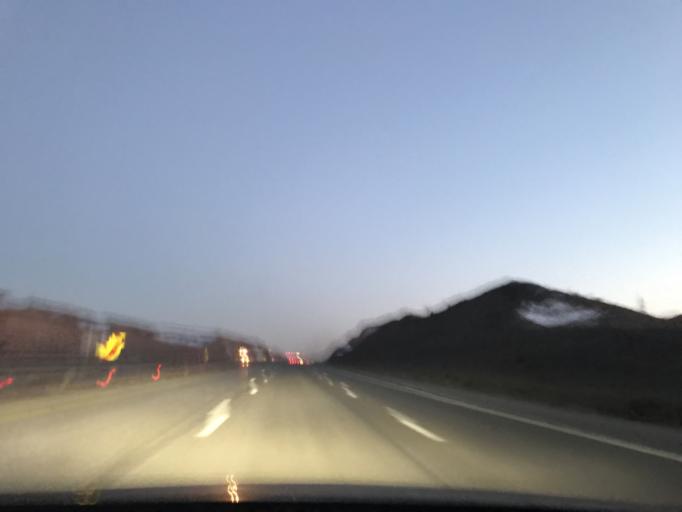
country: IR
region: Isfahan
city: Kashan
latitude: 33.8143
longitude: 51.6403
